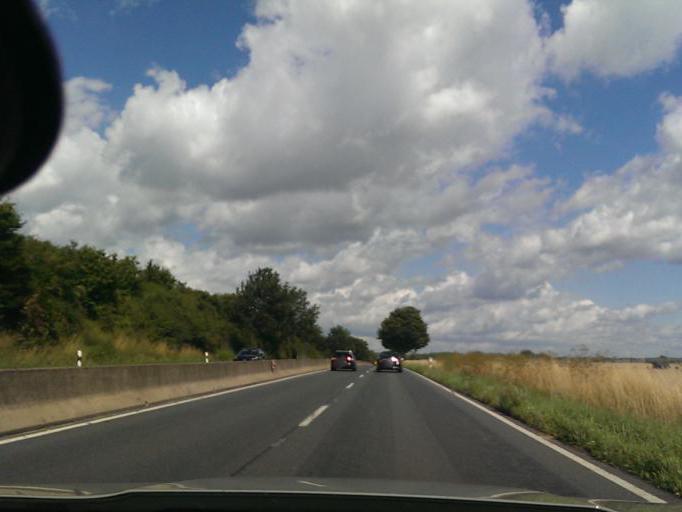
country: DE
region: Lower Saxony
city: Sarstedt
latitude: 52.2830
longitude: 9.8405
